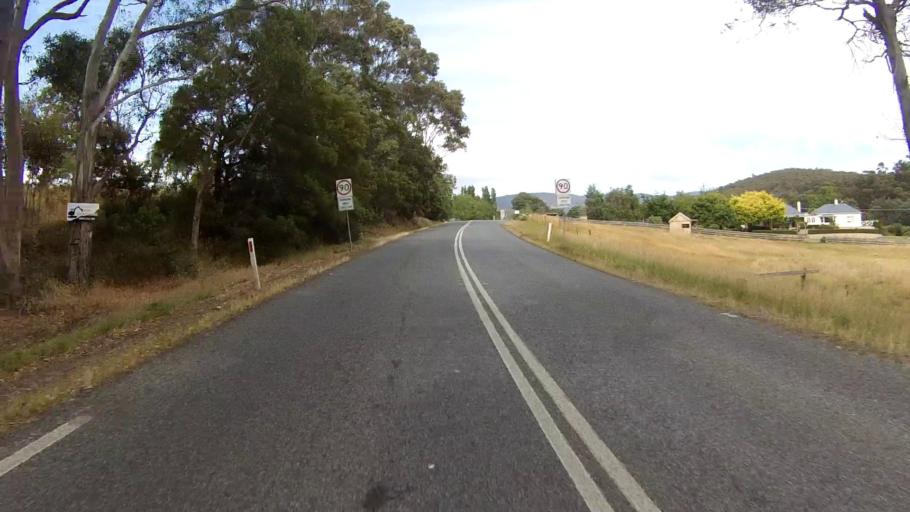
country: AU
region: Tasmania
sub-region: Kingborough
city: Kettering
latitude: -43.1339
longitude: 147.2512
